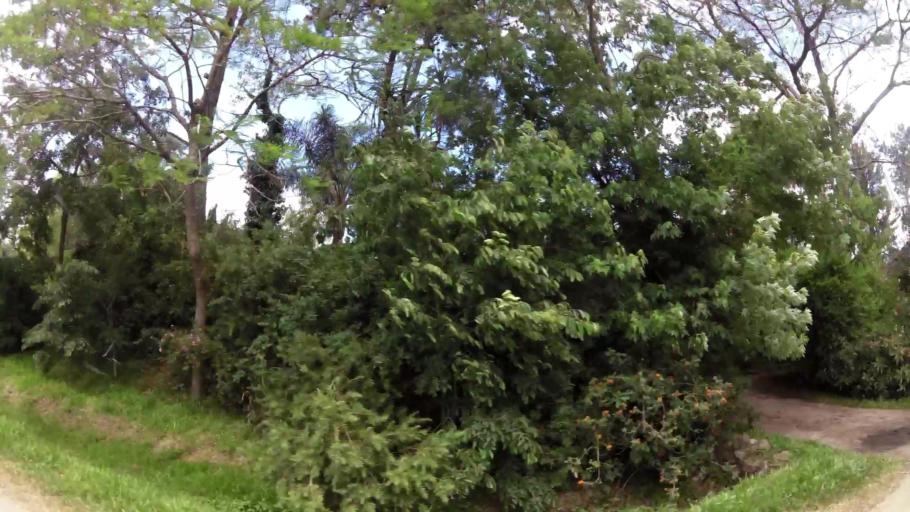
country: UY
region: Canelones
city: Empalme Olmos
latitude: -34.7942
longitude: -55.8828
